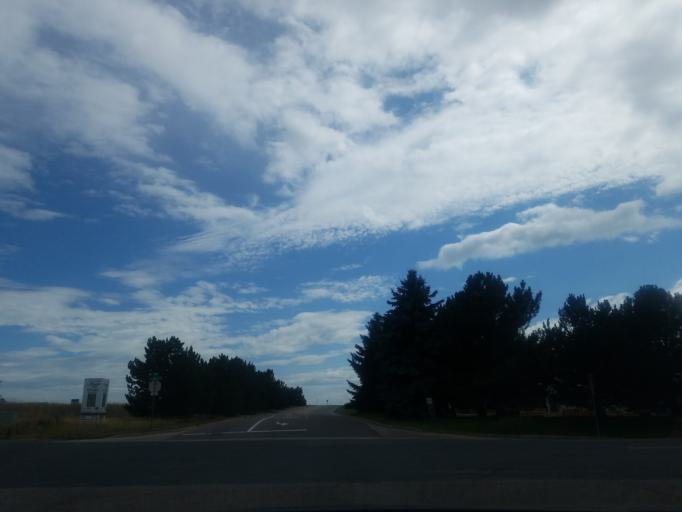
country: US
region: Colorado
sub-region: Larimer County
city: Loveland
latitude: 40.4505
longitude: -104.9941
